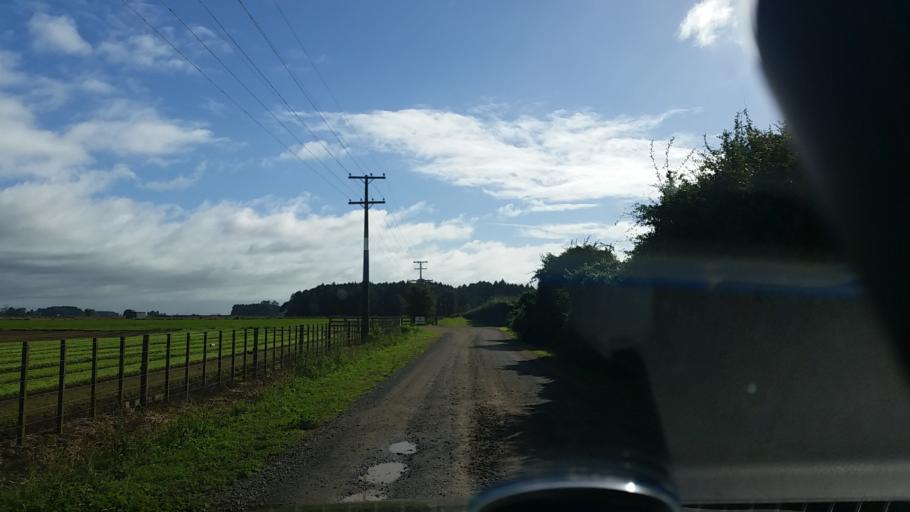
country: NZ
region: Waikato
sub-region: Matamata-Piako District
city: Matamata
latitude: -37.7369
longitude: 175.7542
